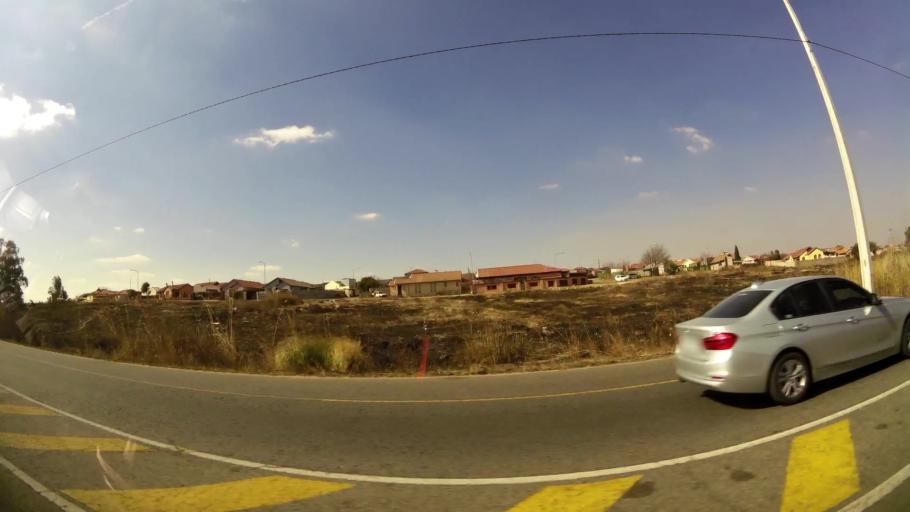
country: ZA
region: Gauteng
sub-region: West Rand District Municipality
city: Krugersdorp
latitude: -26.1516
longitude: 27.7627
